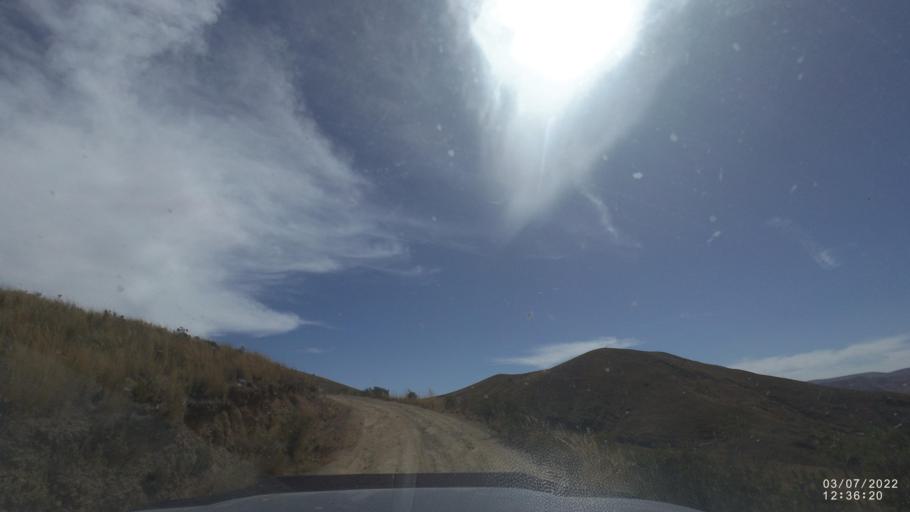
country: BO
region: Cochabamba
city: Irpa Irpa
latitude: -17.8020
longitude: -66.6122
